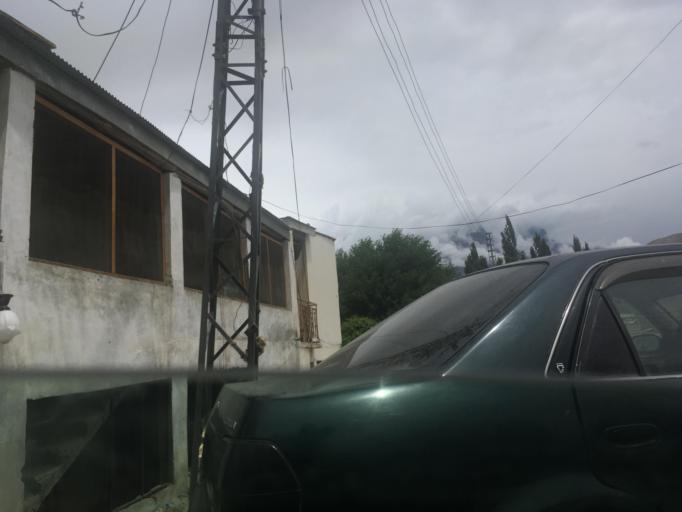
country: PK
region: Gilgit-Baltistan
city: Skardu
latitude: 35.2900
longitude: 75.6444
